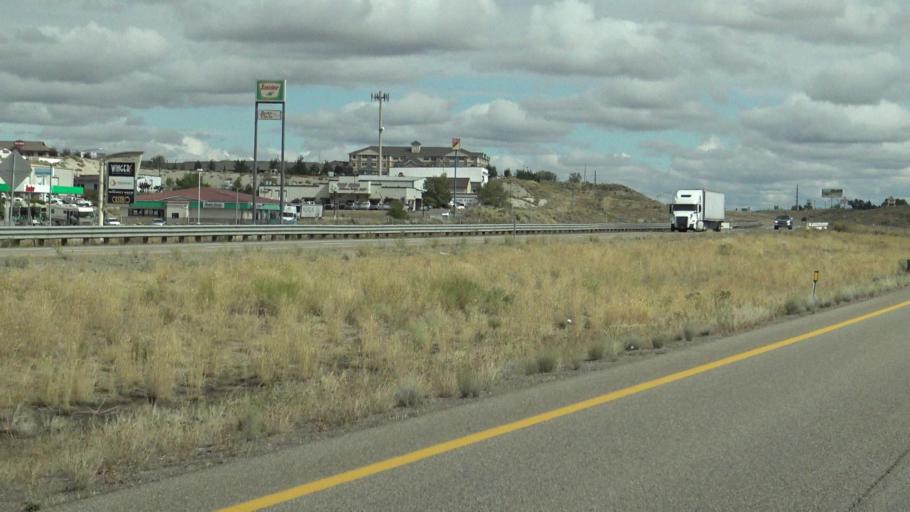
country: US
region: Nevada
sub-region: Elko County
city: Elko
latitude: 40.8510
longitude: -115.7494
